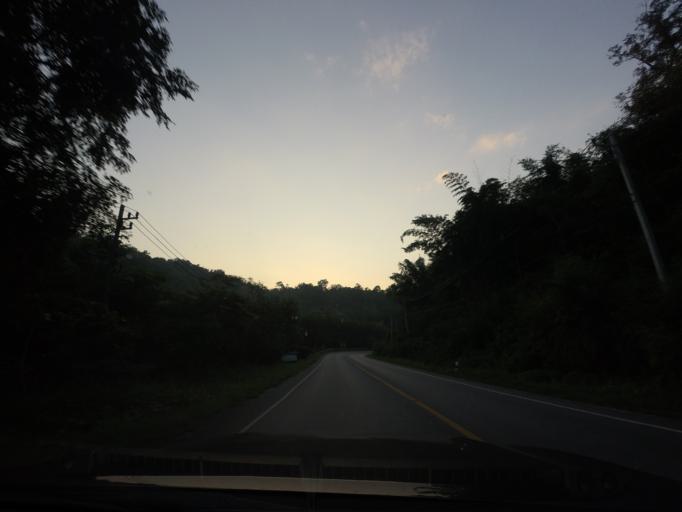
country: TH
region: Nan
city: Na Noi
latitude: 18.4083
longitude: 100.7011
